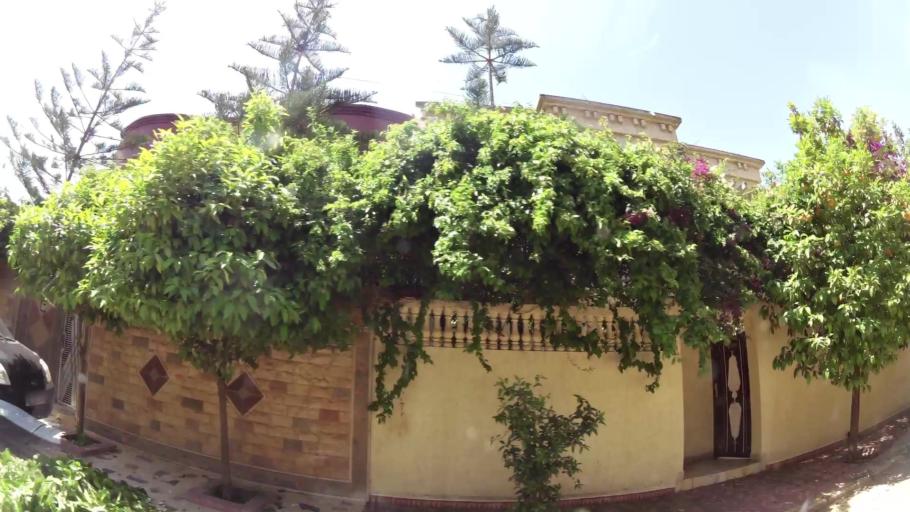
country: MA
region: Rabat-Sale-Zemmour-Zaer
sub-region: Khemisset
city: Khemisset
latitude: 33.8121
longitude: -6.0770
